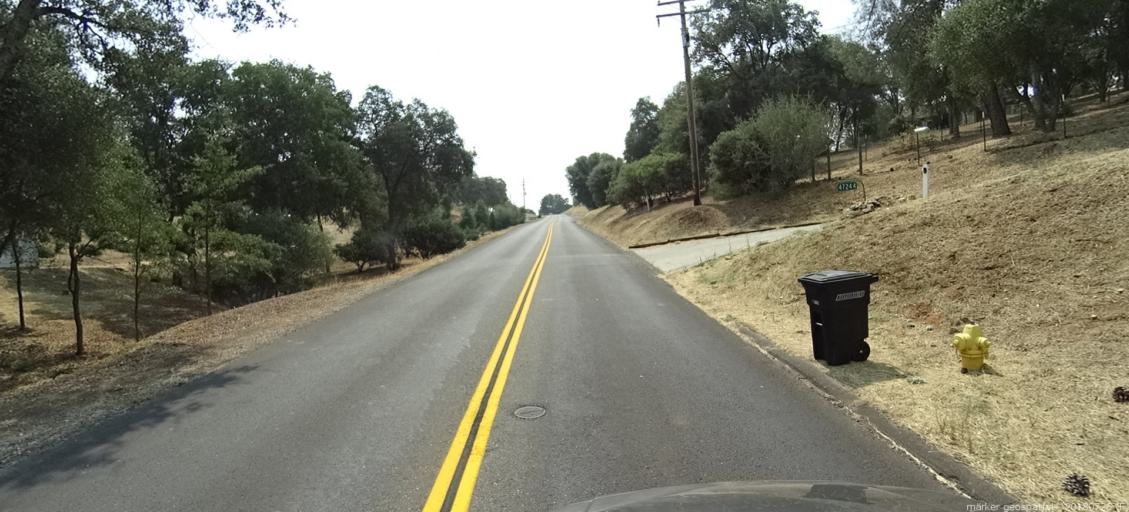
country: US
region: California
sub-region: Madera County
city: Coarsegold
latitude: 37.2457
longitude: -119.6868
